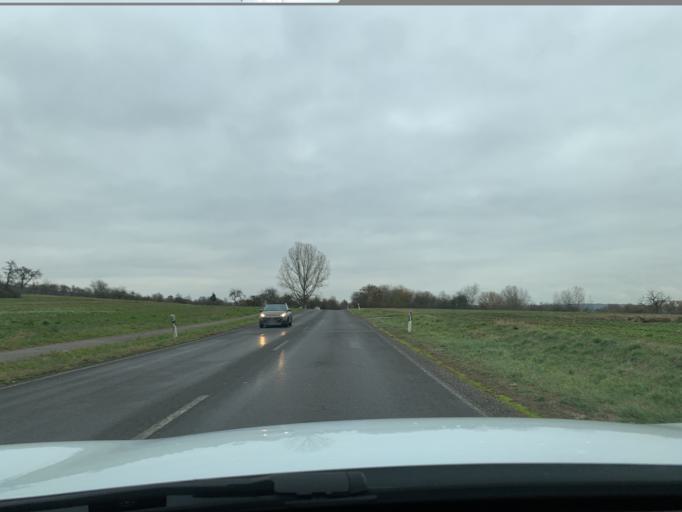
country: DE
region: Saarland
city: Kleinblittersdorf
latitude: 49.1729
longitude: 7.0360
